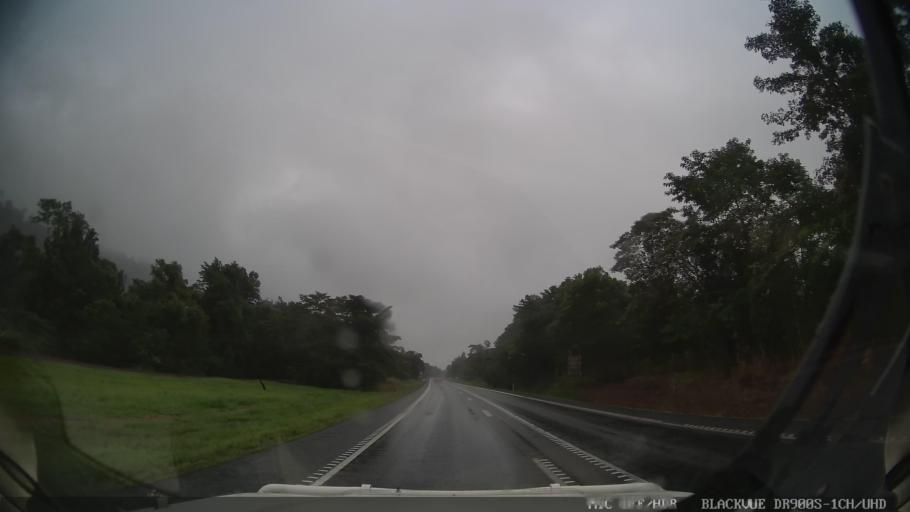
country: AU
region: Queensland
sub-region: Cassowary Coast
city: Innisfail
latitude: -17.8581
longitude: 145.9868
